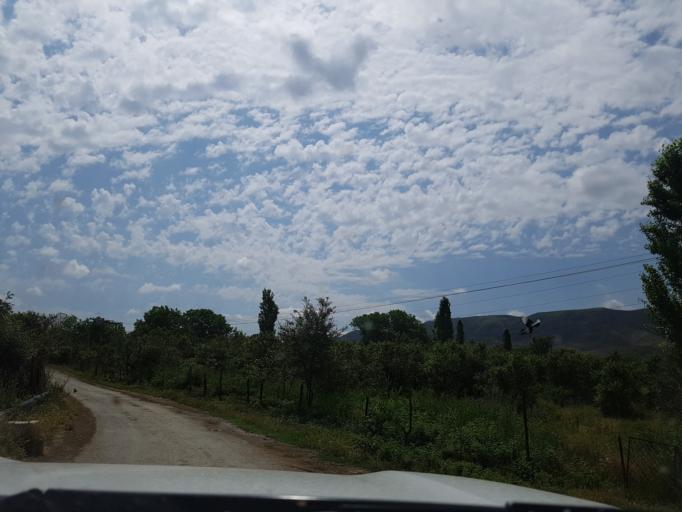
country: TM
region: Ahal
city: Baharly
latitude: 38.2232
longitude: 56.8841
